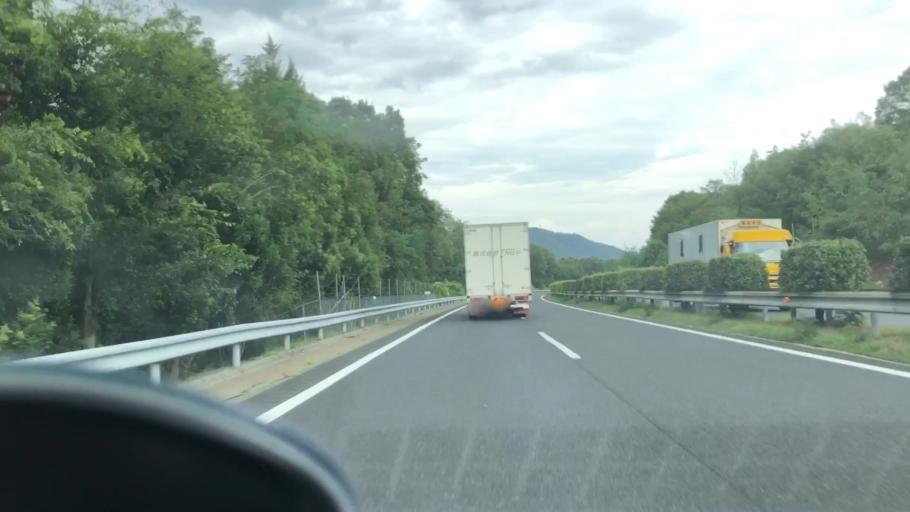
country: JP
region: Hyogo
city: Yashiro
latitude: 34.9332
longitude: 134.9177
